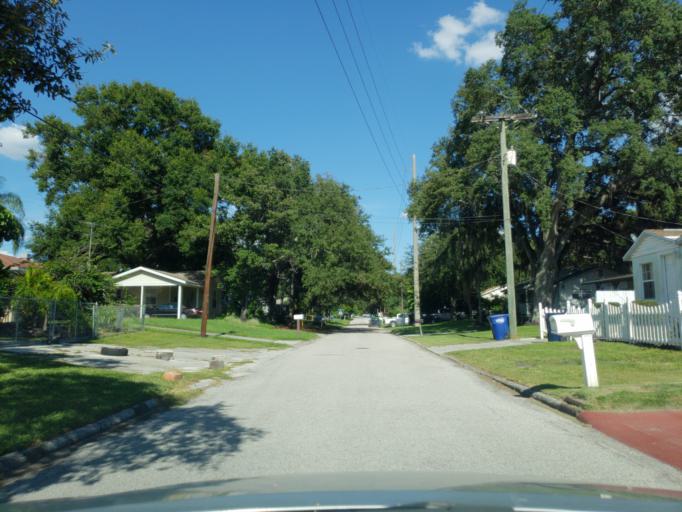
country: US
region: Florida
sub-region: Hillsborough County
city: Tampa
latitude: 27.9543
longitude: -82.4987
